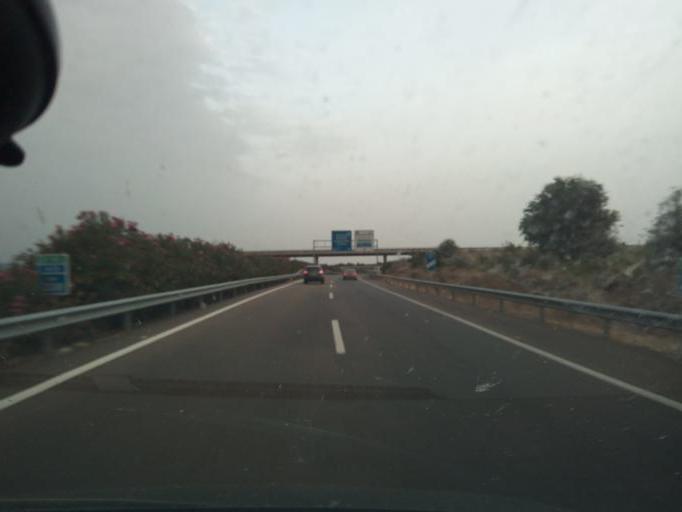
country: ES
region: Extremadura
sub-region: Provincia de Badajoz
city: Merida
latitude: 38.9463
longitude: -6.3281
